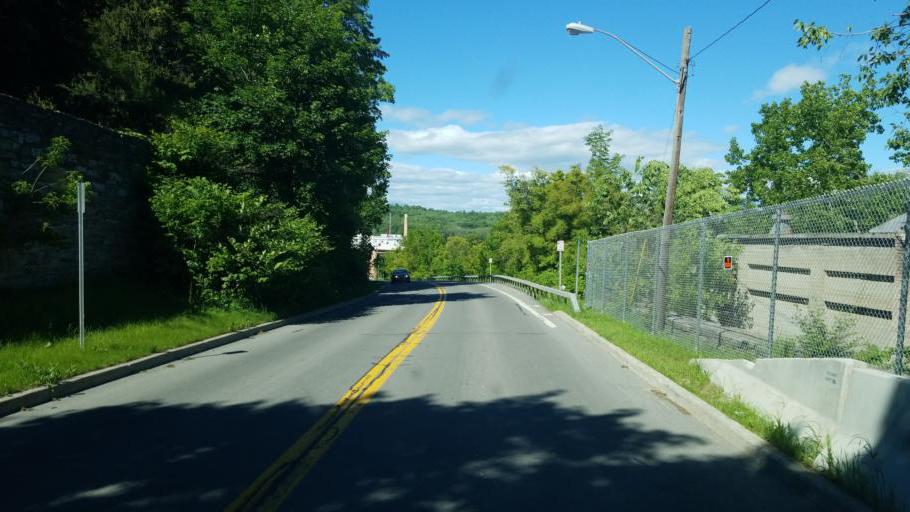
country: US
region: New York
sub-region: Montgomery County
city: Canajoharie
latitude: 42.9028
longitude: -74.5747
